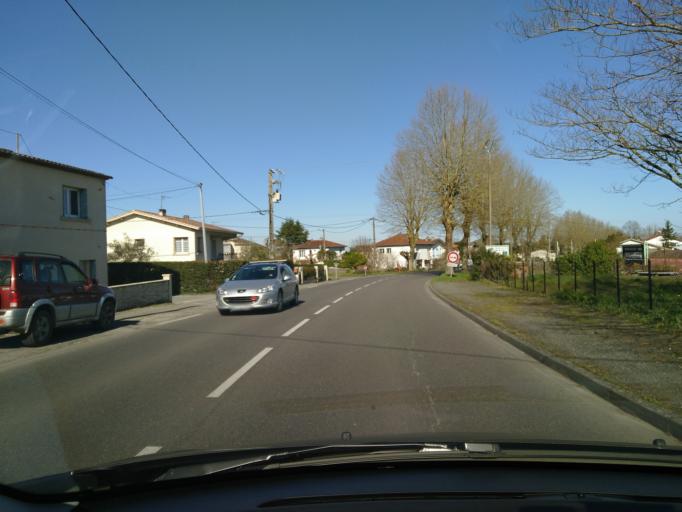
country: FR
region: Aquitaine
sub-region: Departement du Lot-et-Garonne
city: Cancon
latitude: 44.5381
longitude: 0.6217
